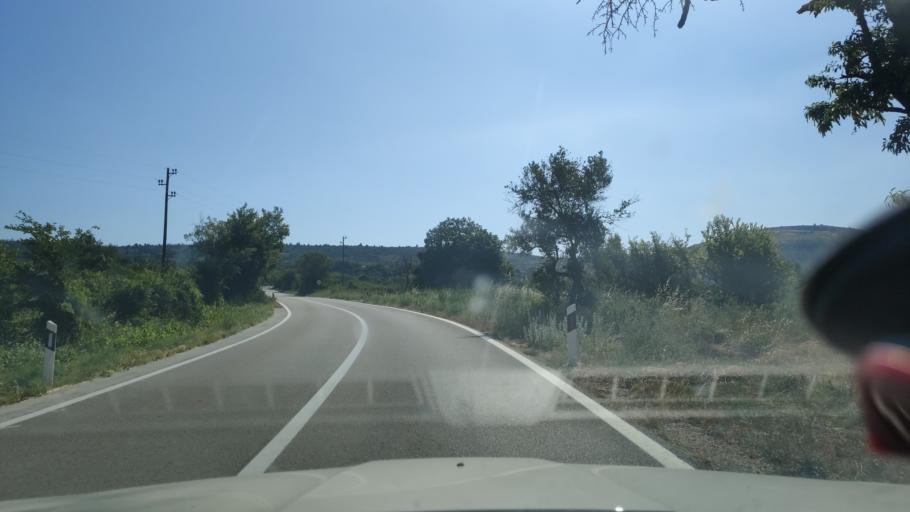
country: HR
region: Sibensko-Kniniska
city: Zaton
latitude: 43.9303
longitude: 15.8229
